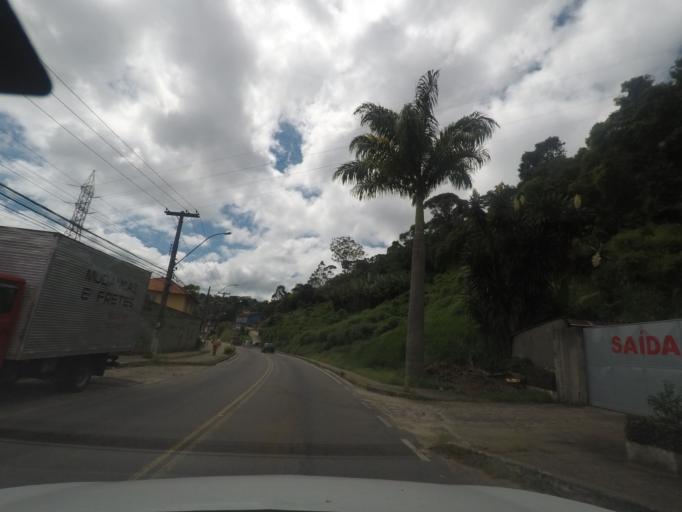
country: BR
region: Rio de Janeiro
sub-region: Teresopolis
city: Teresopolis
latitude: -22.4003
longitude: -42.9815
